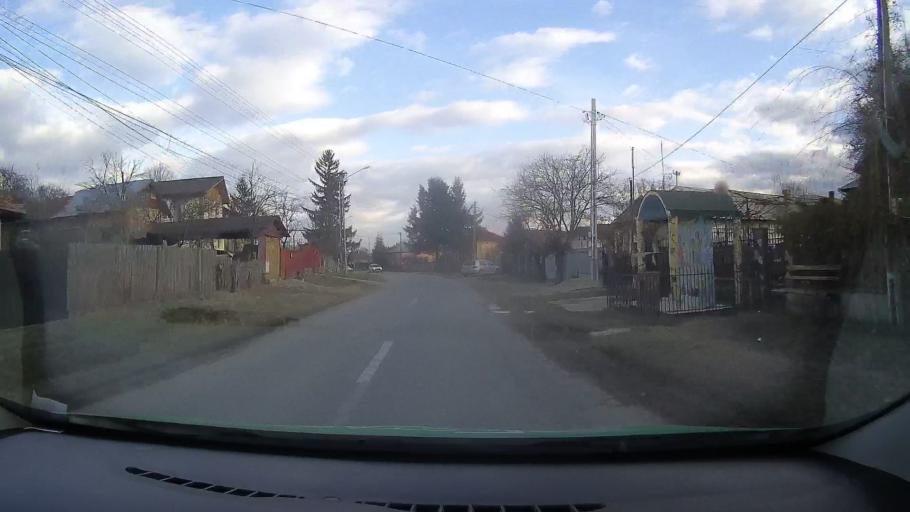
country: RO
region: Dambovita
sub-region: Comuna Gura Ocnitei
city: Gura Ocnitei
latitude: 44.9401
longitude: 25.5692
